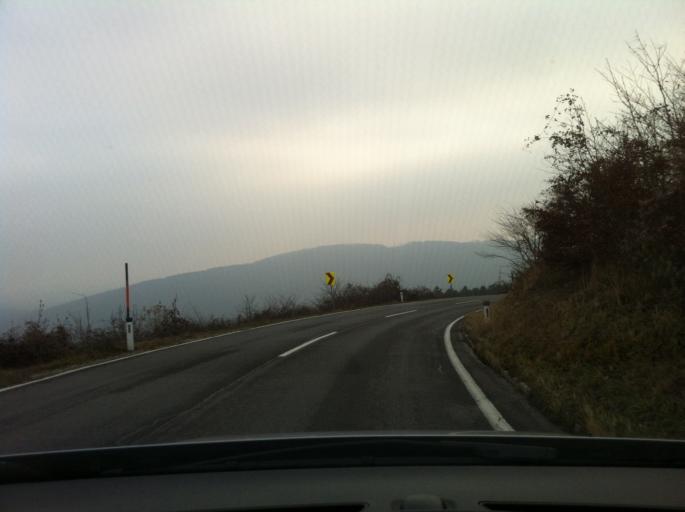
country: AT
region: Lower Austria
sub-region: Politischer Bezirk Wien-Umgebung
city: Mauerbach
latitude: 48.2470
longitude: 16.2558
